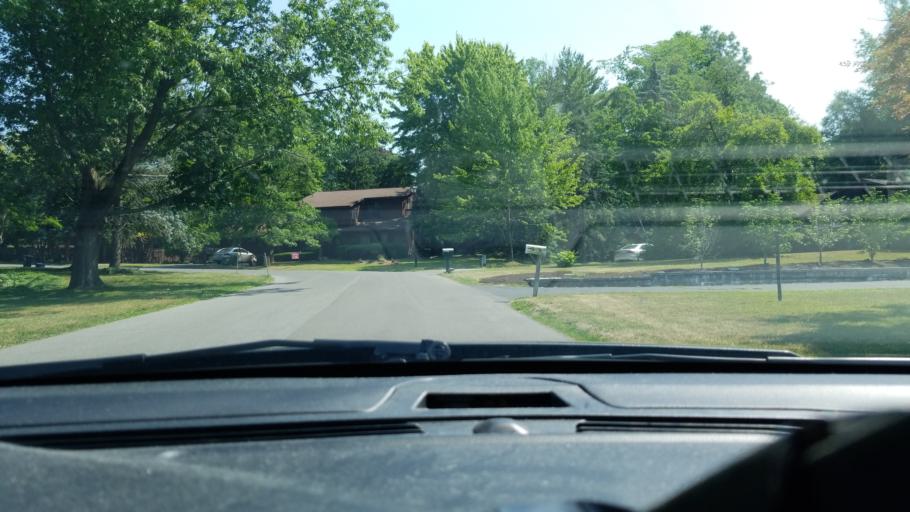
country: US
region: New York
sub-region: Onondaga County
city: Liverpool
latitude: 43.1092
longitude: -76.2217
